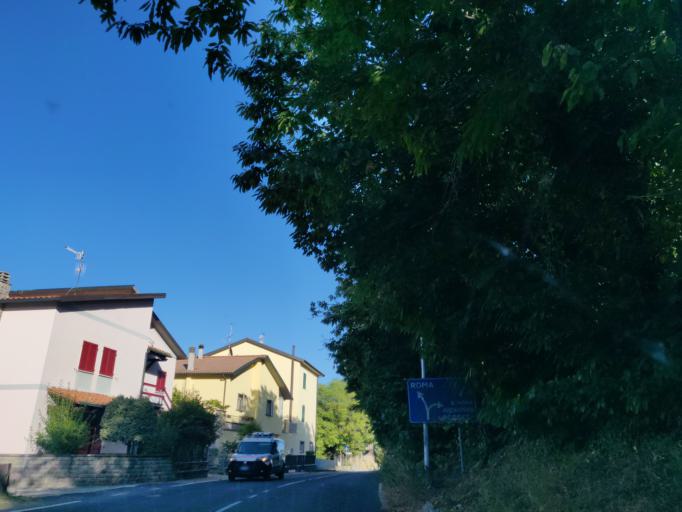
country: IT
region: Tuscany
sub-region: Provincia di Siena
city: Piancastagnaio
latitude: 42.8529
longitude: 11.6854
